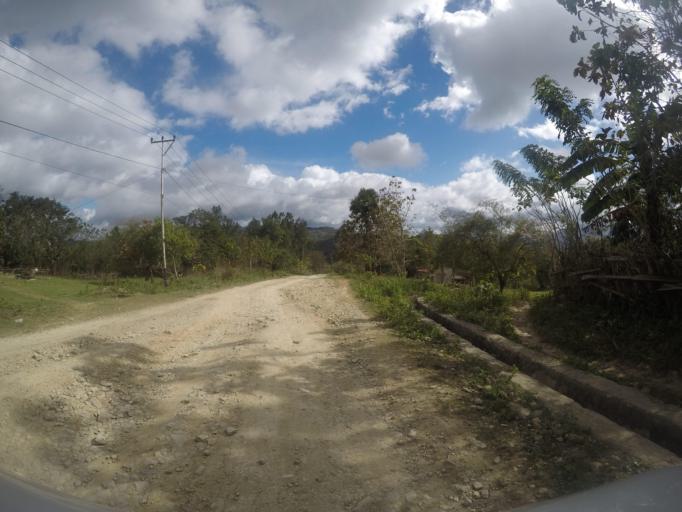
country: TL
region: Lautem
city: Lospalos
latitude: -8.5531
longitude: 126.8971
